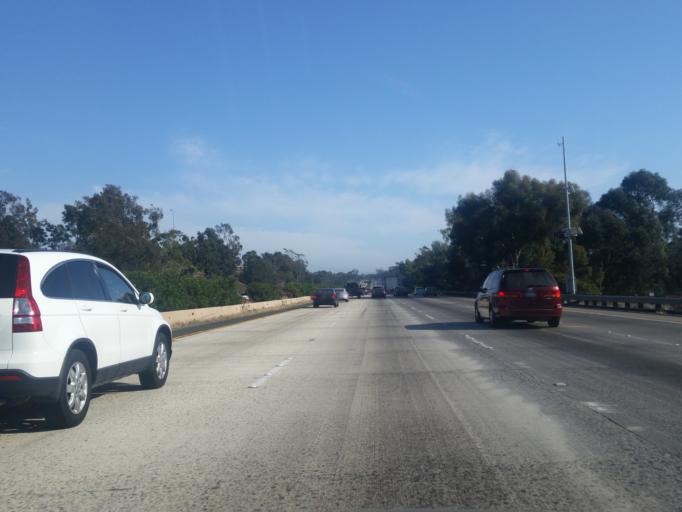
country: US
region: California
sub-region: San Diego County
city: Encinitas
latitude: 33.0560
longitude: -117.2896
